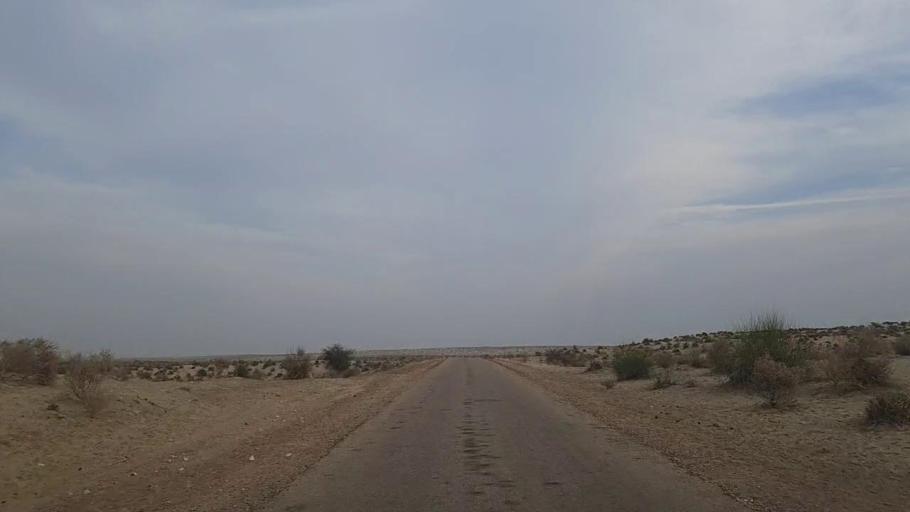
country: PK
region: Sindh
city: Daur
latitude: 26.5148
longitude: 68.4999
